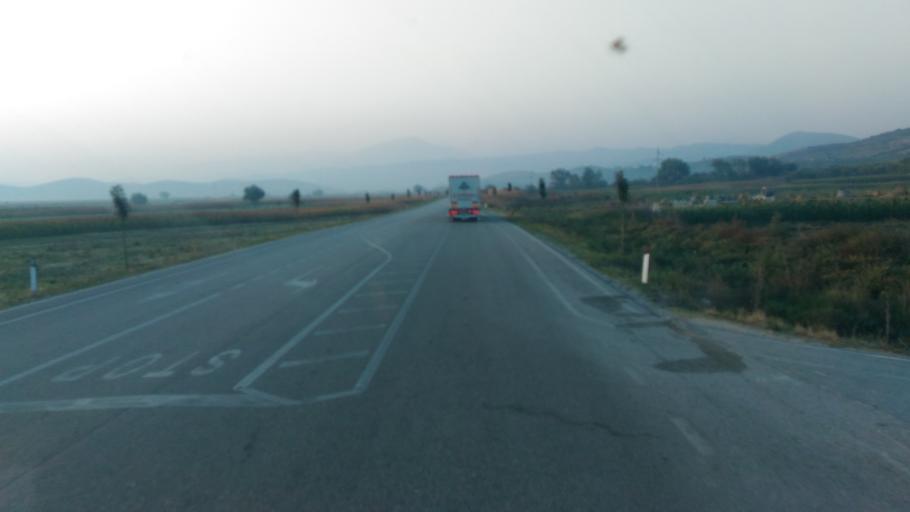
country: AL
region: Fier
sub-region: Rrethi i Fierit
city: Cakran
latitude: 40.5796
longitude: 19.6204
